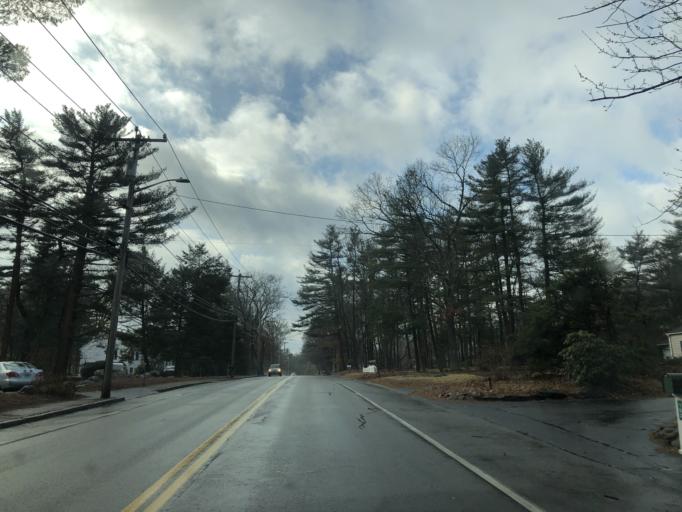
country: US
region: Massachusetts
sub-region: Bristol County
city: Attleboro
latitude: 41.9841
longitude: -71.2912
